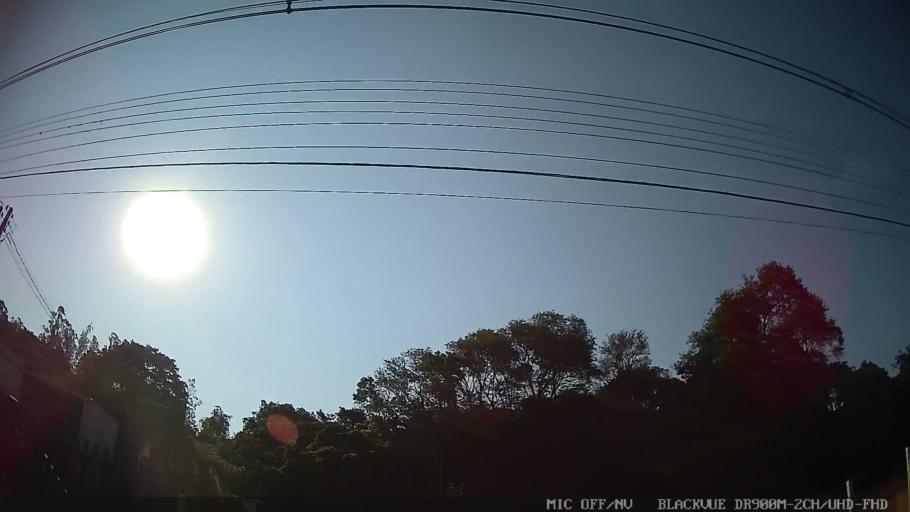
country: BR
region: Sao Paulo
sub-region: Itatiba
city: Itatiba
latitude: -22.9922
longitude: -46.8486
